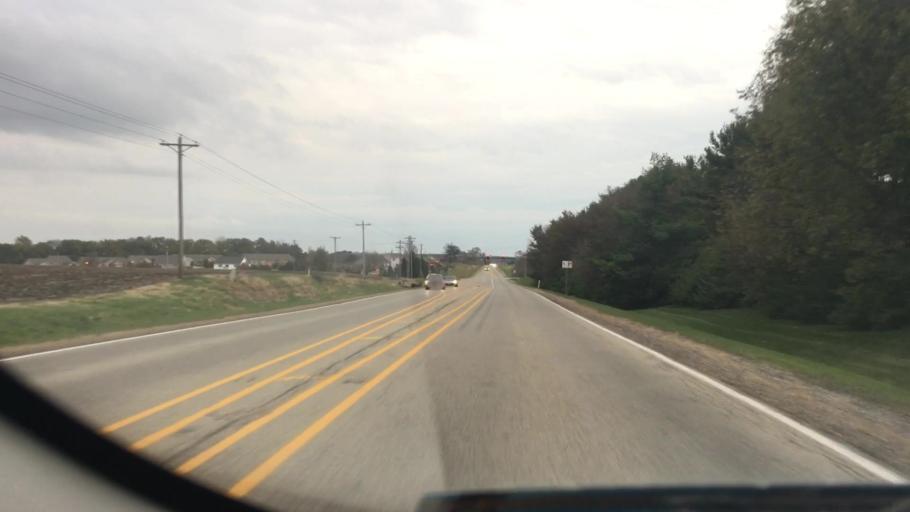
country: US
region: Illinois
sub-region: McLean County
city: Normal
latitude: 40.5112
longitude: -89.0360
